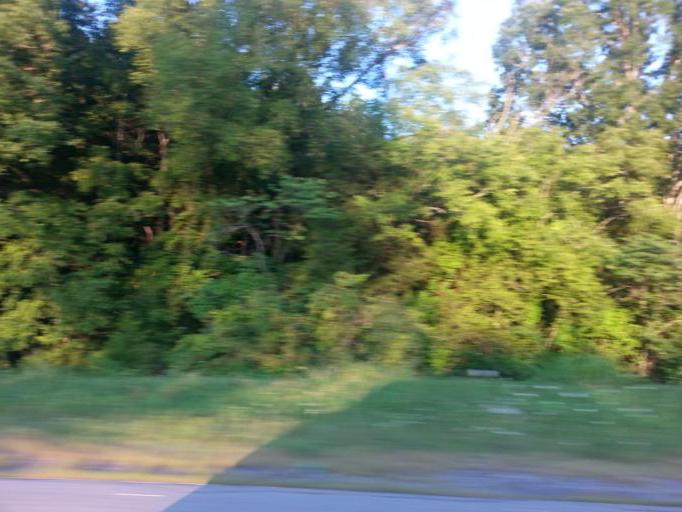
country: US
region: Tennessee
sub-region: Union County
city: Luttrell
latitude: 36.1813
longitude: -83.7408
